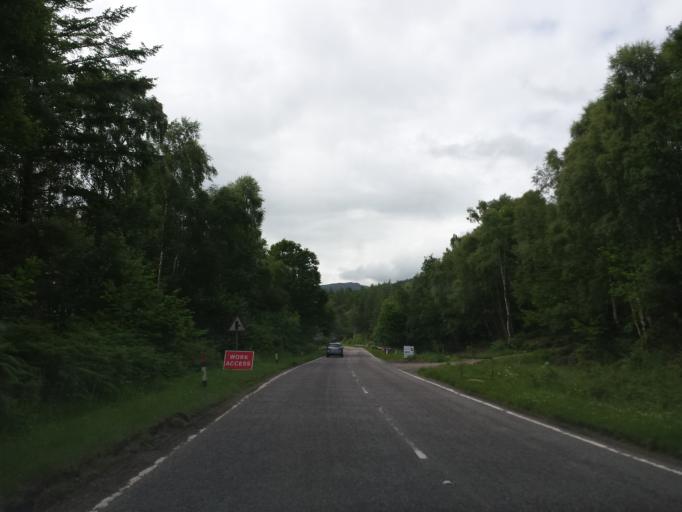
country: GB
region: Scotland
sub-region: Highland
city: Fort William
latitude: 56.8540
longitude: -5.1870
